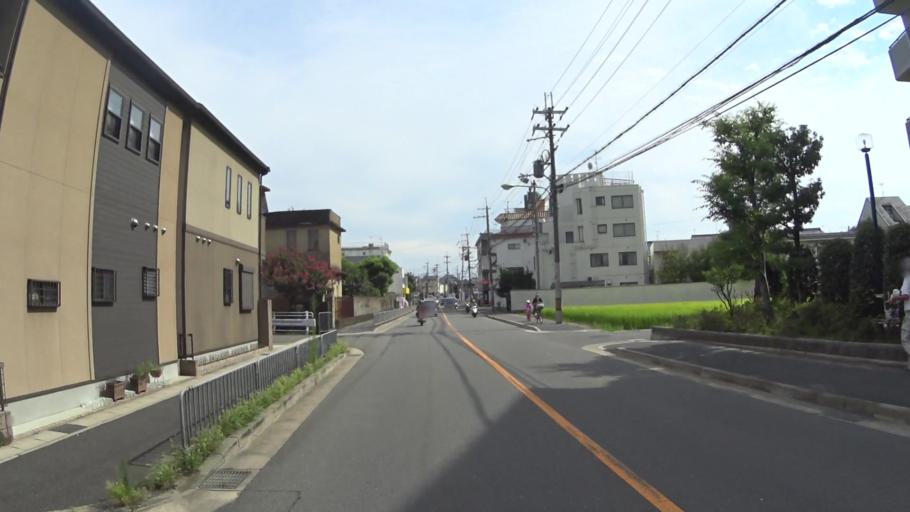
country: JP
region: Kyoto
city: Muko
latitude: 34.9980
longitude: 135.6885
